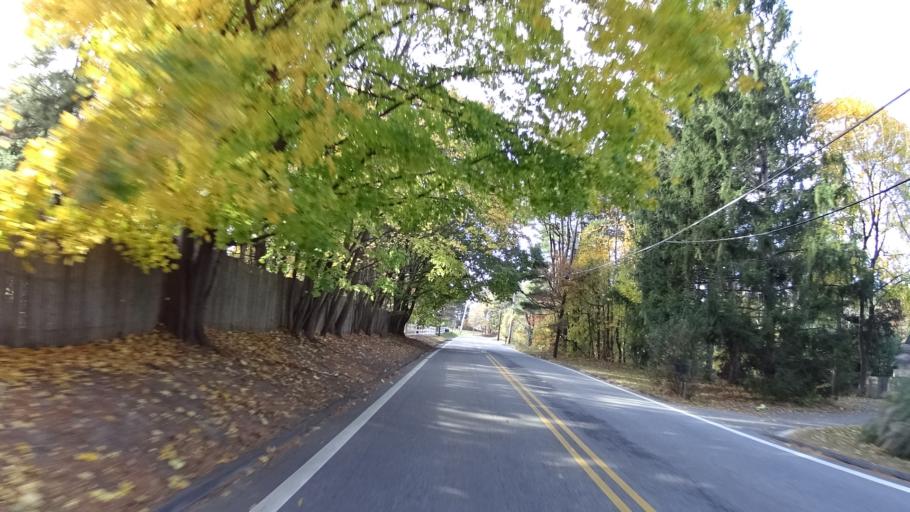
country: US
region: New Jersey
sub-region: Morris County
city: Morristown
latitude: 40.7462
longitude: -74.5024
